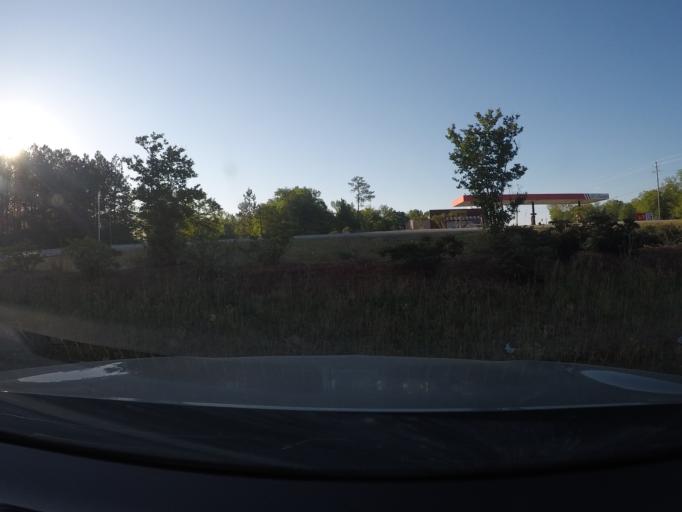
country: US
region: Georgia
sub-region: Bulloch County
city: Statesboro
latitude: 32.4951
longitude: -81.8152
